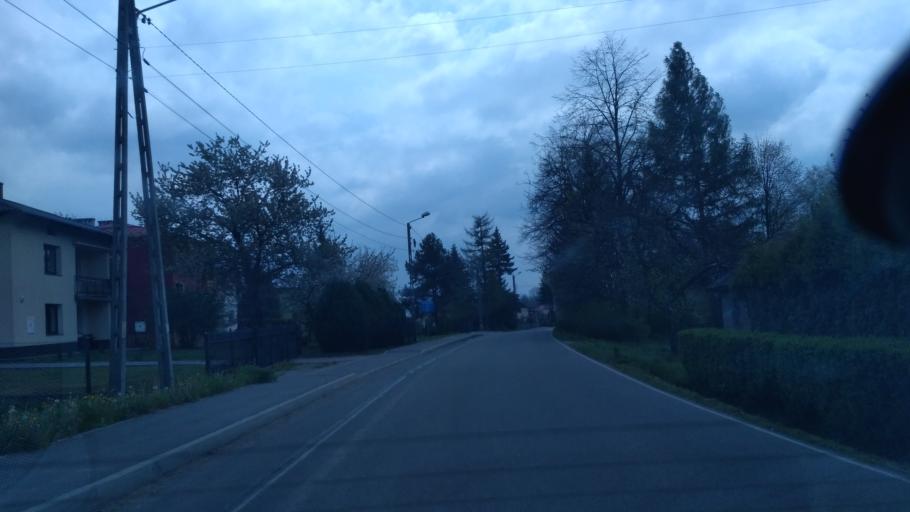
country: PL
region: Subcarpathian Voivodeship
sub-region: Powiat brzozowski
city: Haczow
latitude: 49.6570
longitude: 21.9094
